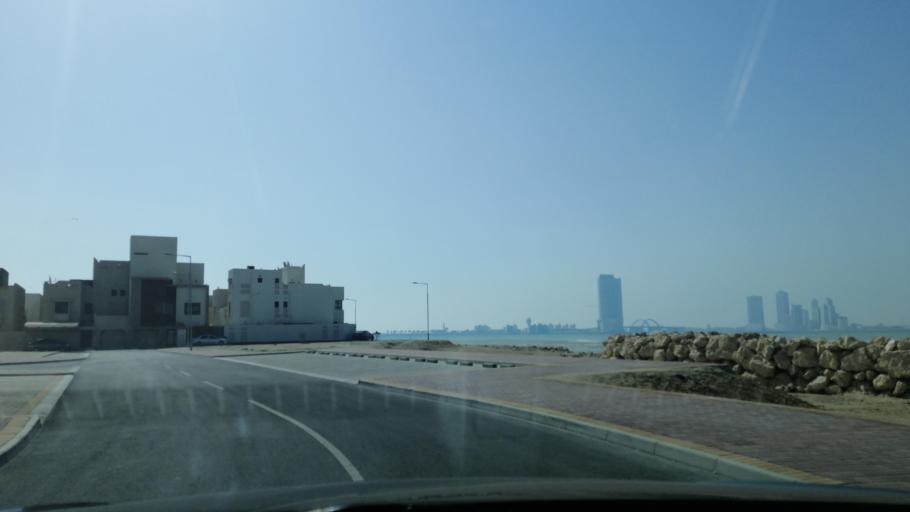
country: BH
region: Muharraq
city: Al Hadd
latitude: 26.2400
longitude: 50.6337
